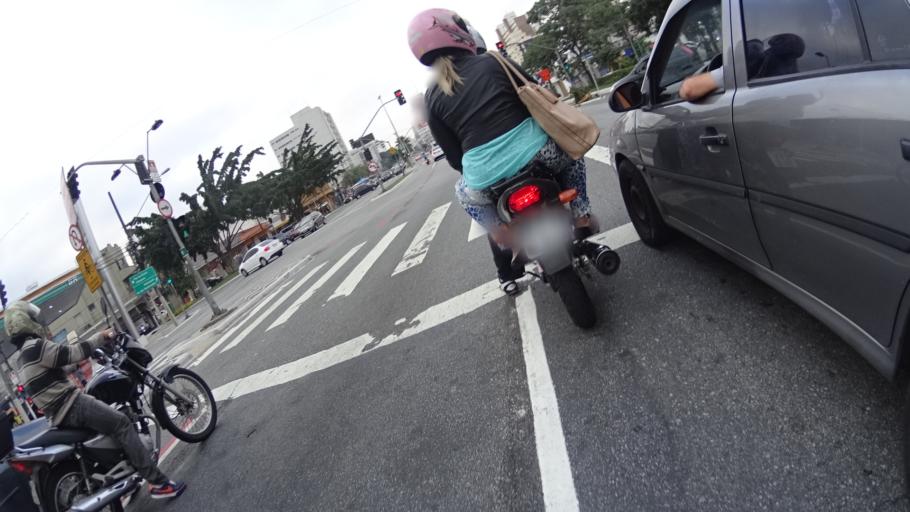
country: BR
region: Sao Paulo
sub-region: Sao Paulo
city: Sao Paulo
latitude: -23.6047
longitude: -46.6366
